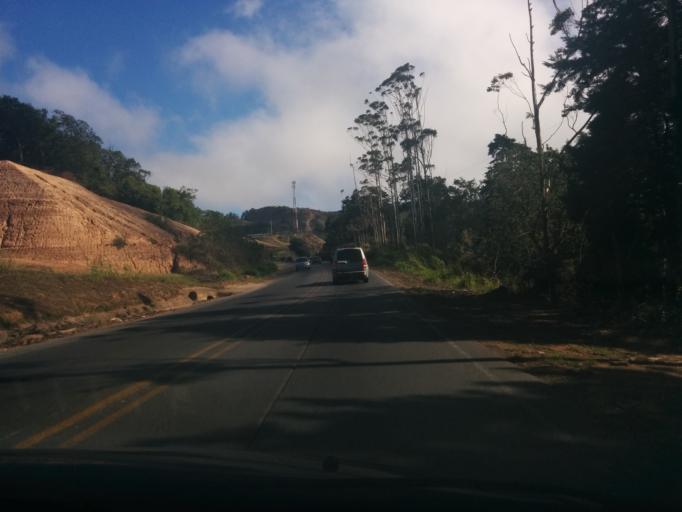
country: CR
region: Alajuela
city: San Rafael
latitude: 10.0633
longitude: -84.4993
